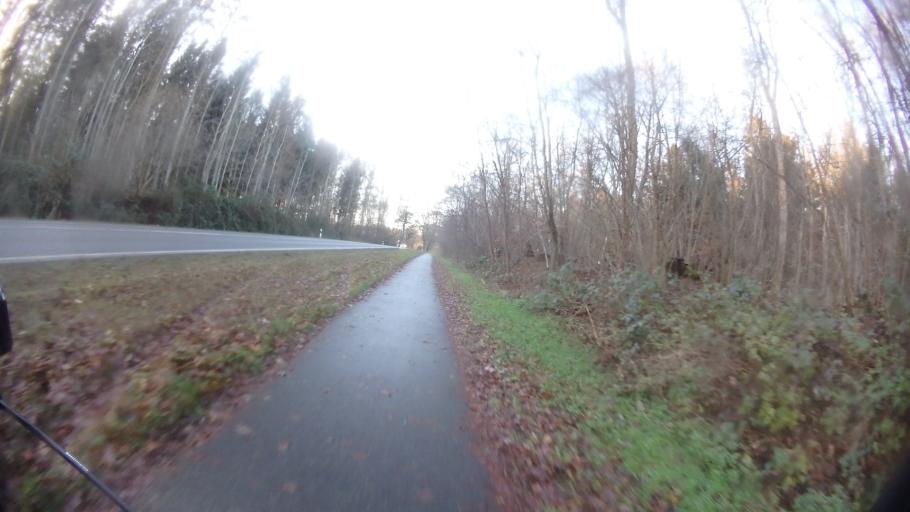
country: DE
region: Schleswig-Holstein
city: Ratekau
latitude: 53.9995
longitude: 10.7025
